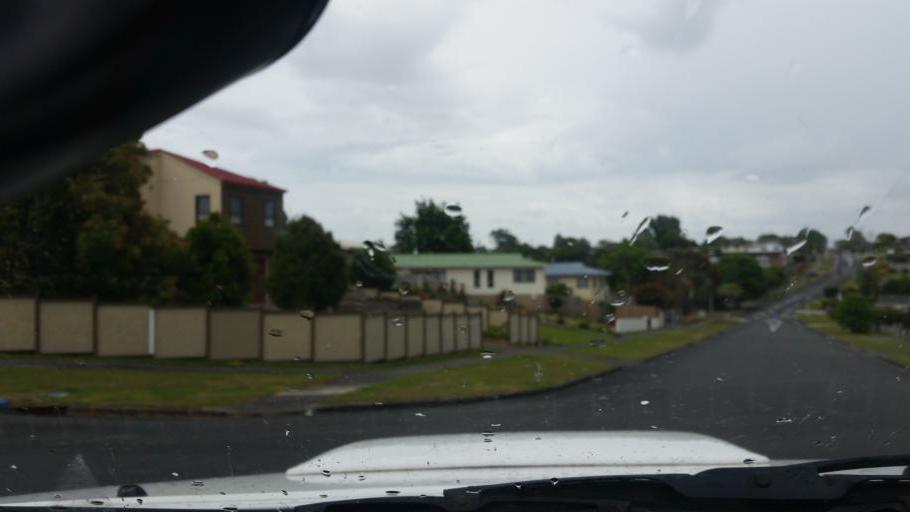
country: NZ
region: Northland
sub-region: Kaipara District
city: Dargaville
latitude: -35.9291
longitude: 173.8641
